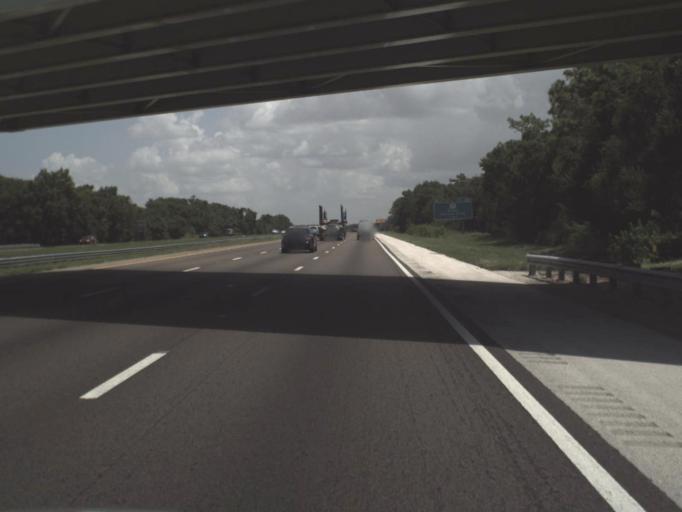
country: US
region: Florida
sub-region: Hillsborough County
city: Ruskin
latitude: 27.6981
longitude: -82.4025
